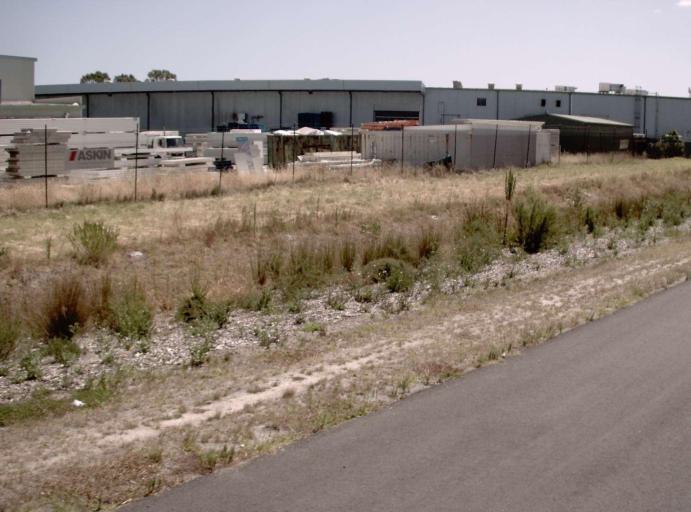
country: AU
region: Victoria
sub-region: Kingston
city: Dingley Village
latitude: -37.9868
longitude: 145.1513
